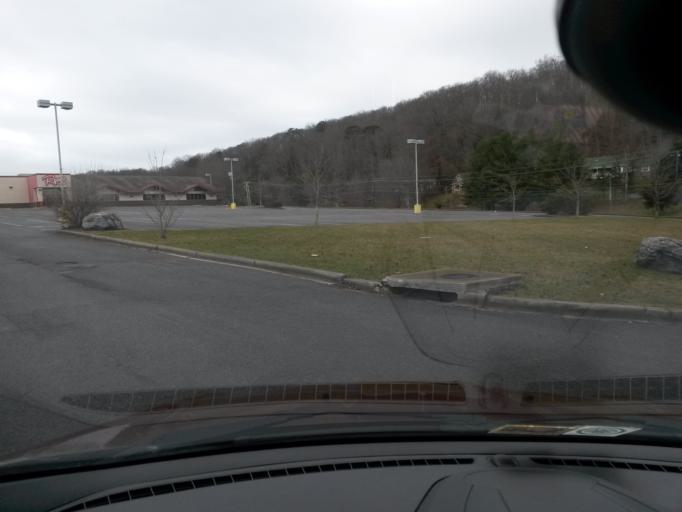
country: US
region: Virginia
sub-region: Tazewell County
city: Bluefield
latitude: 37.2404
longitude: -81.2509
